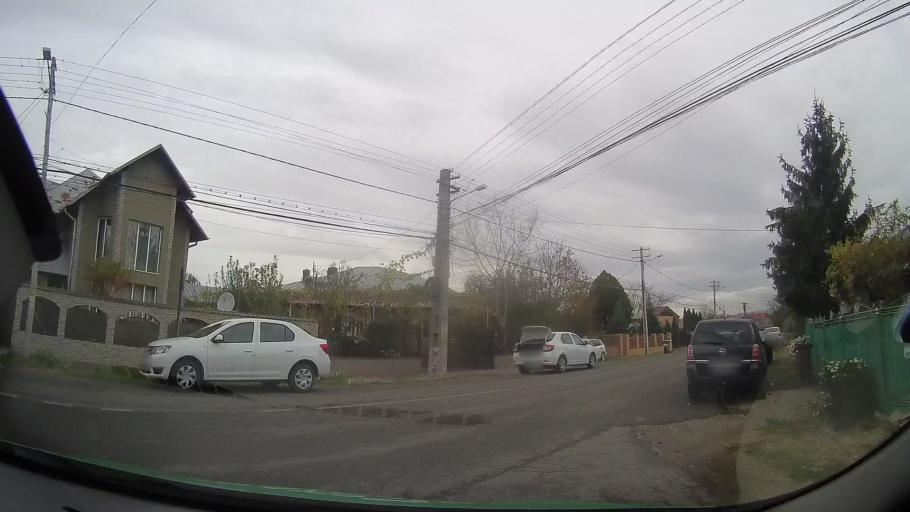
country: RO
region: Prahova
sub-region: Comuna Berceni
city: Berceni
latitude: 44.9318
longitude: 26.1231
